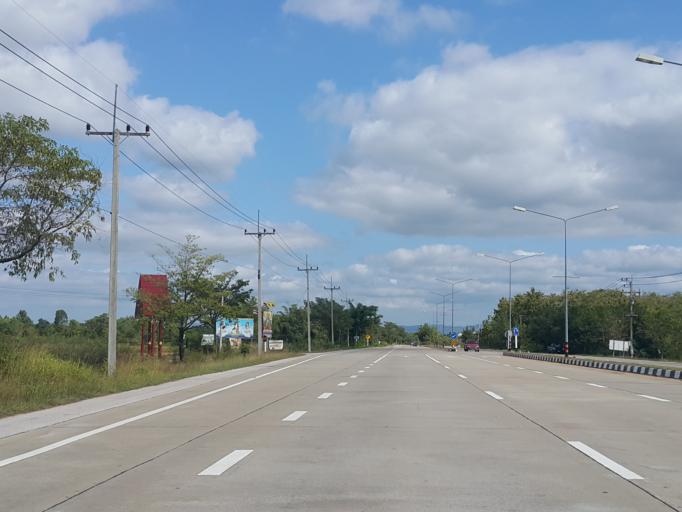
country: TH
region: Lampang
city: Hang Chat
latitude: 18.3272
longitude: 99.4054
